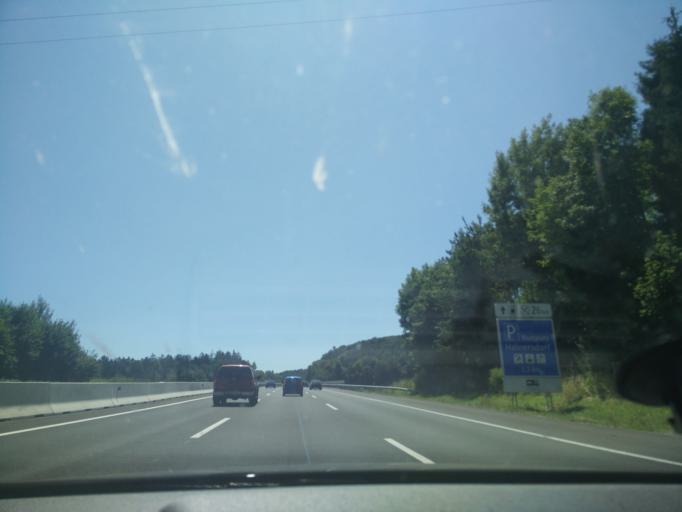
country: AT
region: Styria
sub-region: Politischer Bezirk Hartberg-Fuerstenfeld
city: Bad Waltersdorf
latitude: 47.1687
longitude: 15.9991
